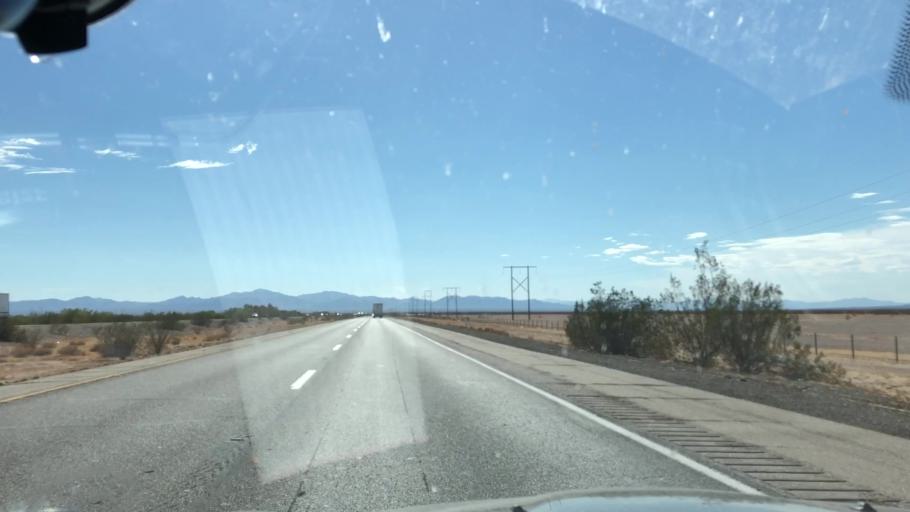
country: US
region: California
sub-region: Riverside County
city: Mesa Verde
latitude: 33.6063
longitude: -114.9359
